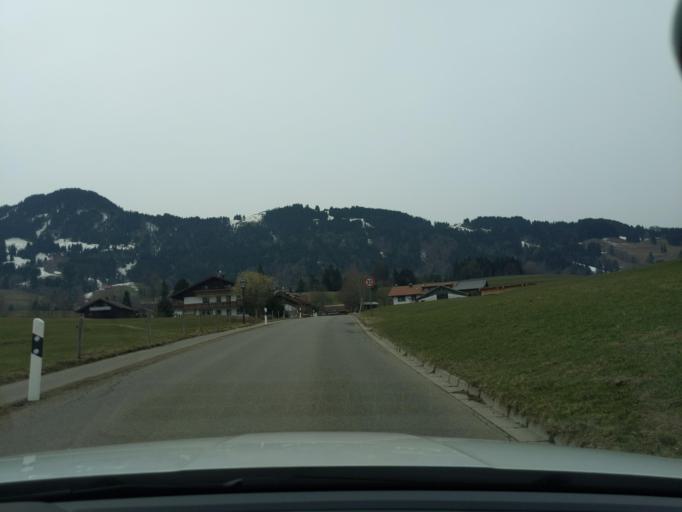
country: DE
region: Bavaria
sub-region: Swabia
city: Ofterschwang
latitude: 47.4892
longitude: 10.2445
